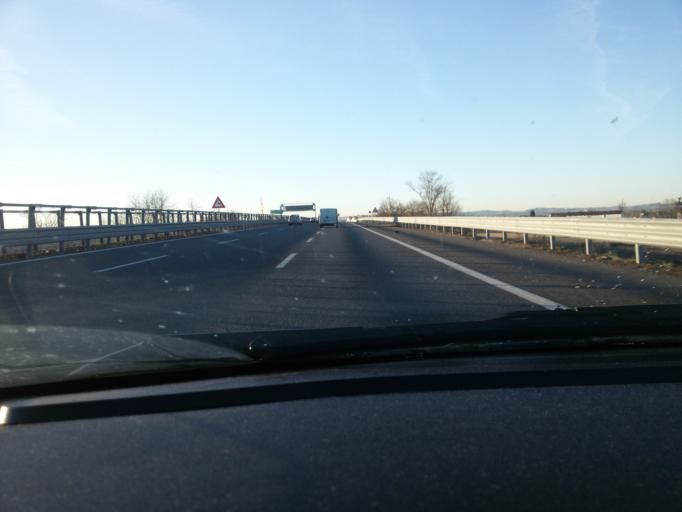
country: IT
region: Piedmont
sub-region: Provincia di Alessandria
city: Borgo San Martino
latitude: 45.1129
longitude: 8.4891
